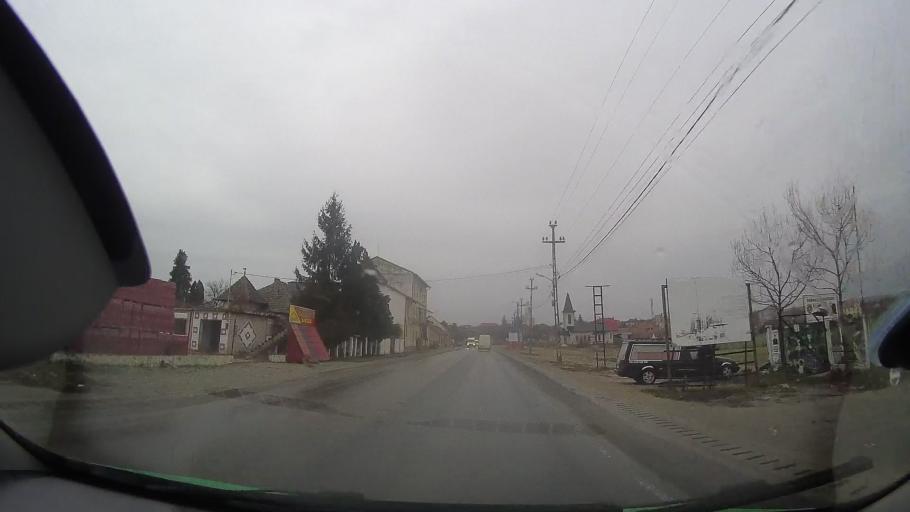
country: RO
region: Bihor
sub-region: Comuna Tinca
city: Tinca
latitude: 46.7697
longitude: 21.9321
